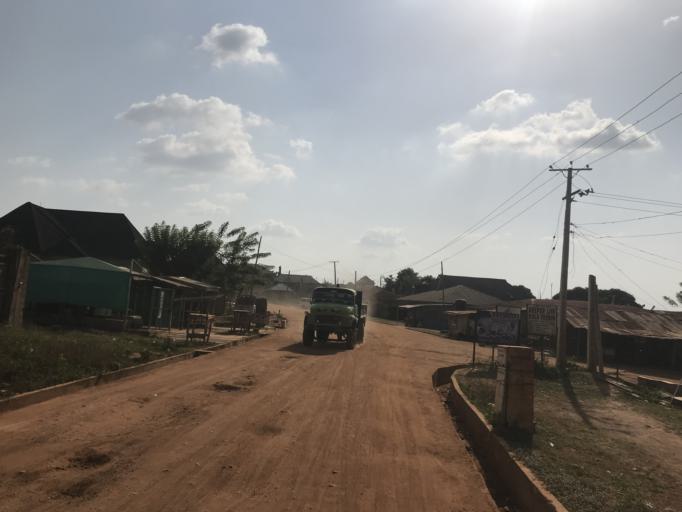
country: NG
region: Osun
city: Osogbo
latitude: 7.8109
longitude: 4.5590
